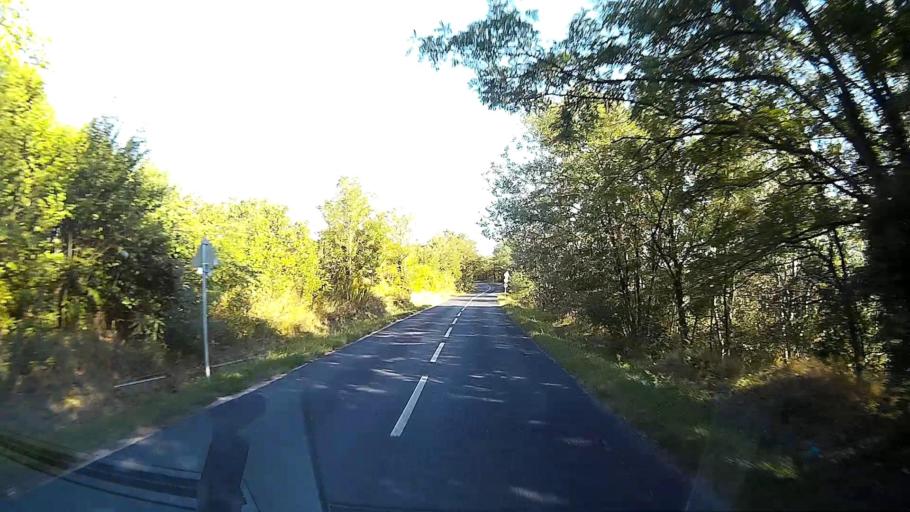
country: HU
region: Pest
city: Csobanka
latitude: 47.6280
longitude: 18.9471
